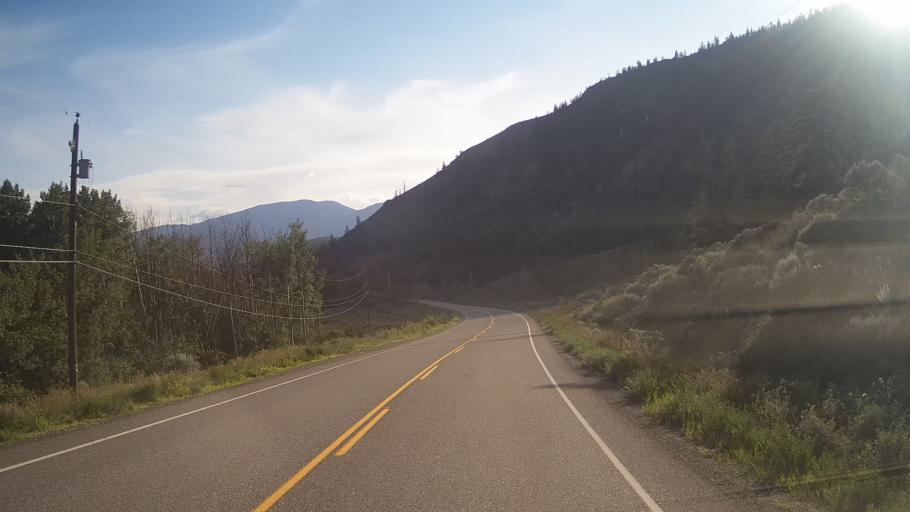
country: CA
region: British Columbia
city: Lillooet
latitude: 50.8941
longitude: -121.8001
